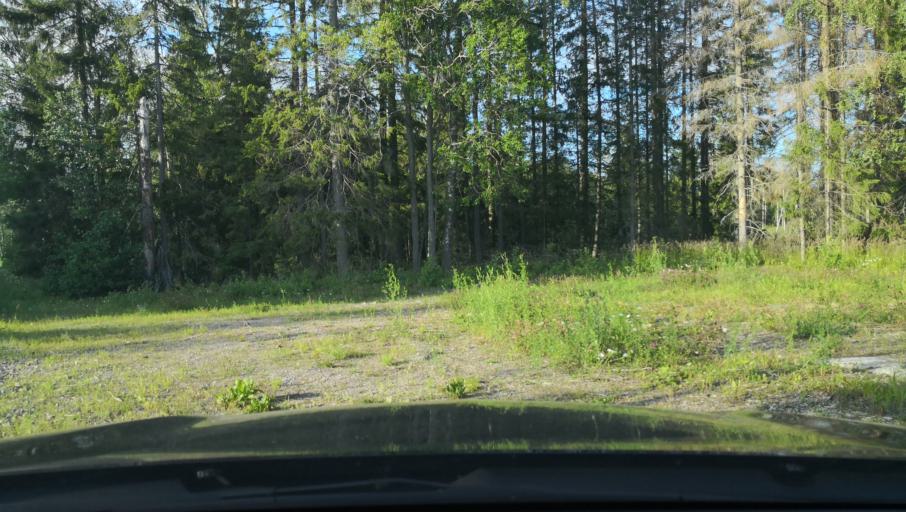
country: SE
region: Uppsala
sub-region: Osthammars Kommun
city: Osterbybruk
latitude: 60.0367
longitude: 17.9194
